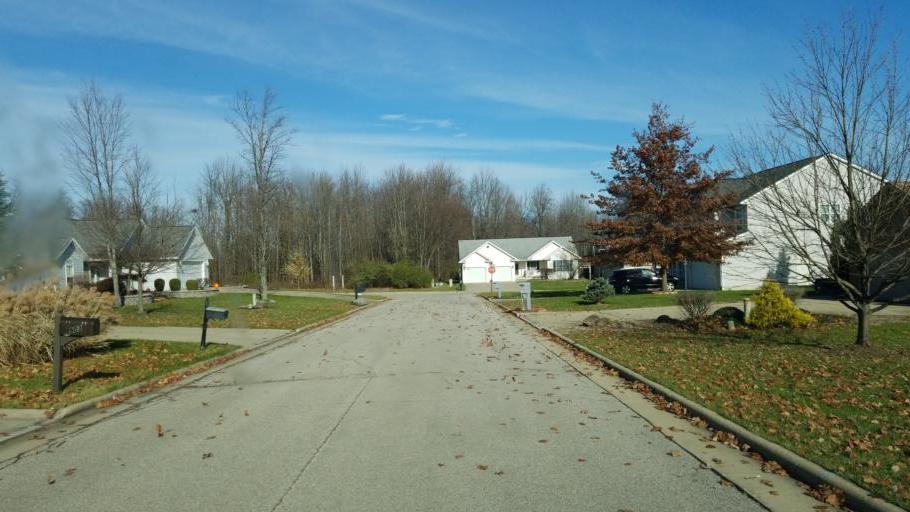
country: US
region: Ohio
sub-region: Richland County
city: Ontario
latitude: 40.7772
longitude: -82.5836
